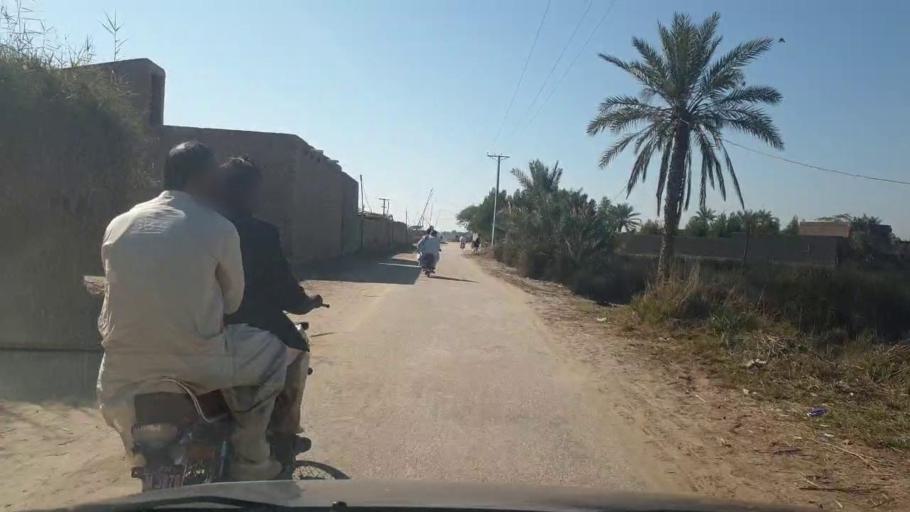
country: PK
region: Sindh
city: Bozdar
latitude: 27.1358
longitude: 68.6433
